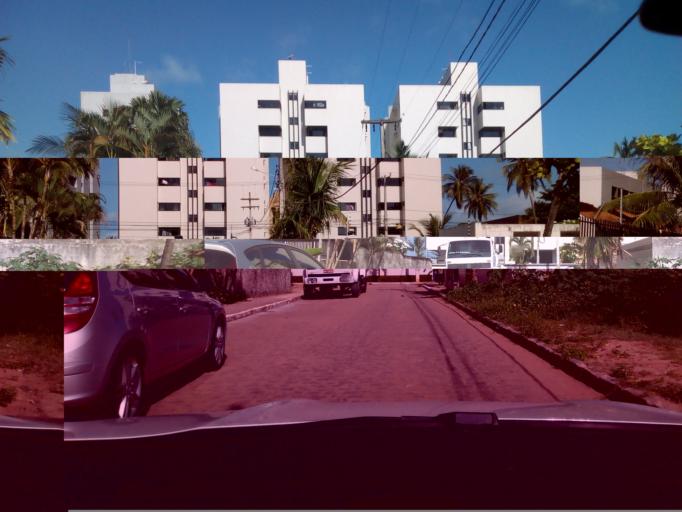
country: BR
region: Paraiba
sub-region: Cabedelo
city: Cabedelo
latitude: -7.0416
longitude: -34.8416
